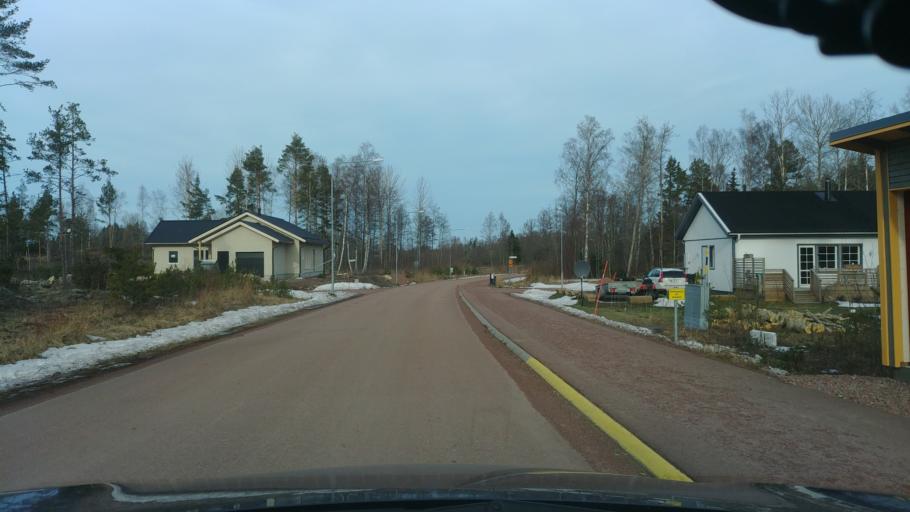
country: AX
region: Mariehamns stad
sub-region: Mariehamn
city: Mariehamn
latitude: 60.1033
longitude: 19.8935
